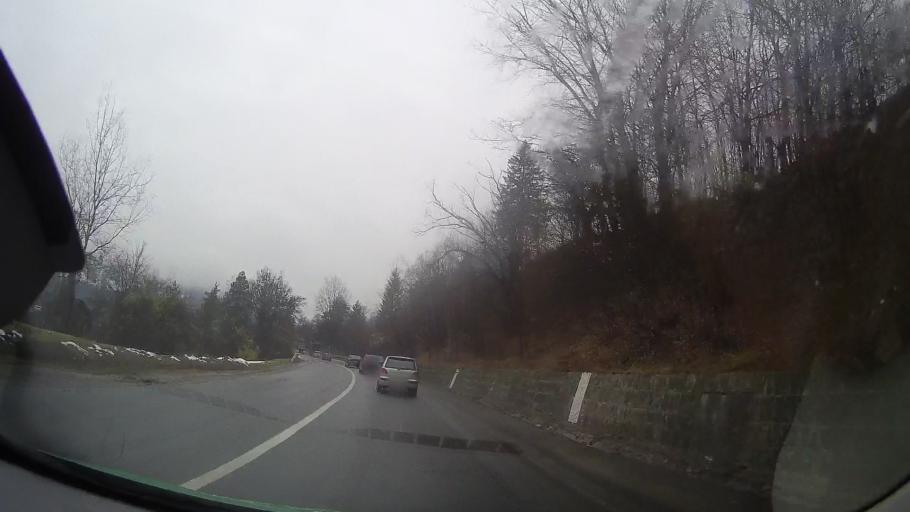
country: RO
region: Neamt
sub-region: Comuna Bicaz
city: Dodeni
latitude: 46.9015
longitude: 26.1174
